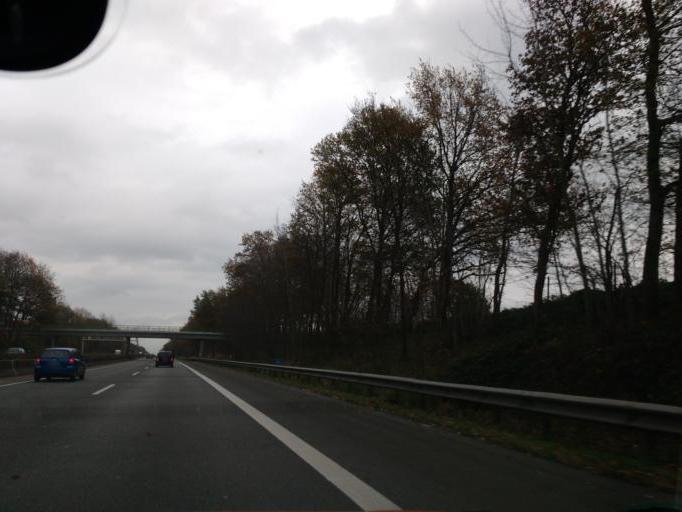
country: DE
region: Lower Saxony
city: Ahsen-Oetzen
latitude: 53.0139
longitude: 9.0912
